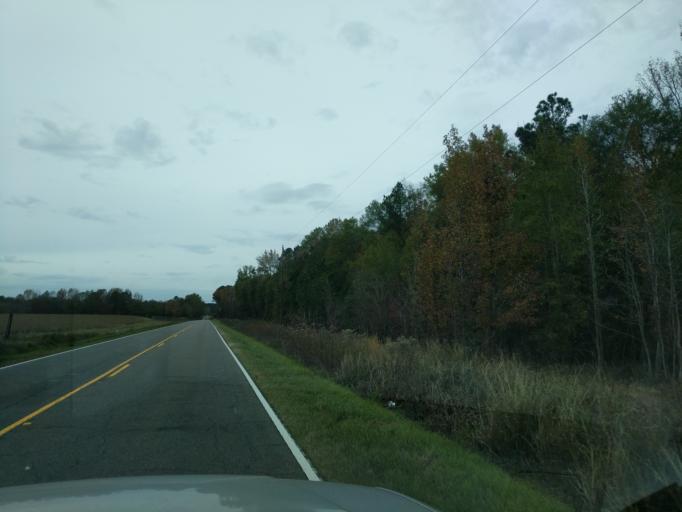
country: US
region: South Carolina
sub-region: Lexington County
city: Batesburg
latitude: 33.9283
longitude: -81.5921
